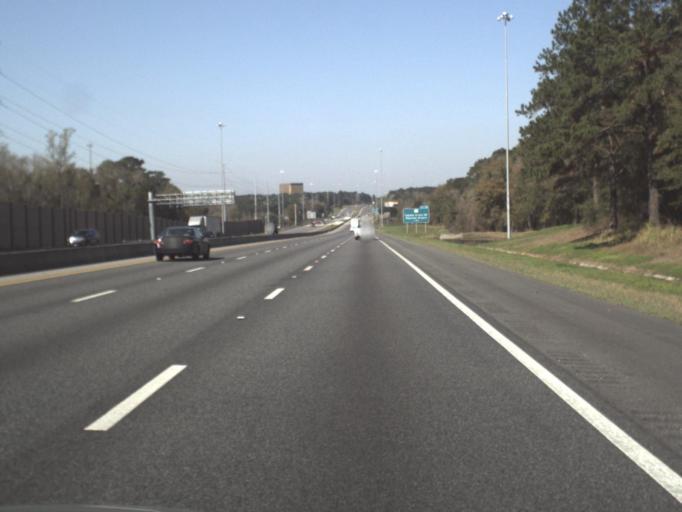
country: US
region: Florida
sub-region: Leon County
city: Tallahassee
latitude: 30.4784
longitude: -84.3385
